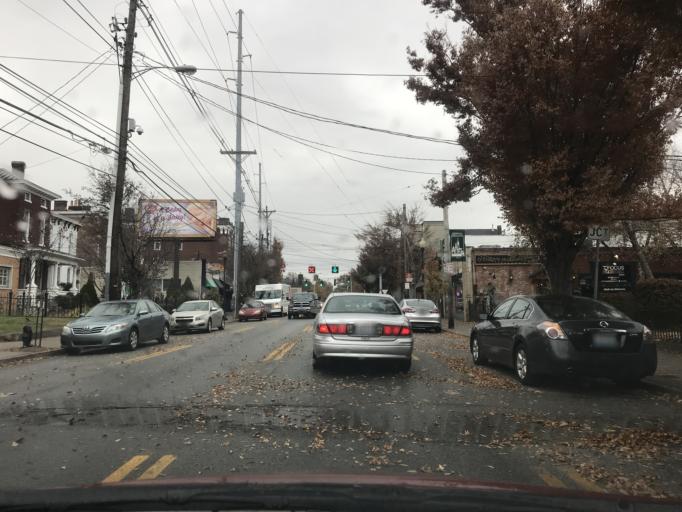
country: US
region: Kentucky
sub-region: Jefferson County
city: Louisville
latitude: 38.2411
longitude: -85.7250
